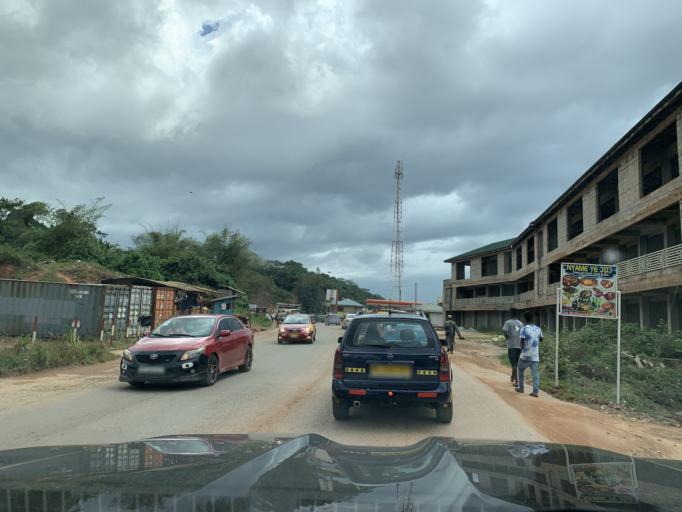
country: GH
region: Western
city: Tarkwa
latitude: 5.3287
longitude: -1.9809
